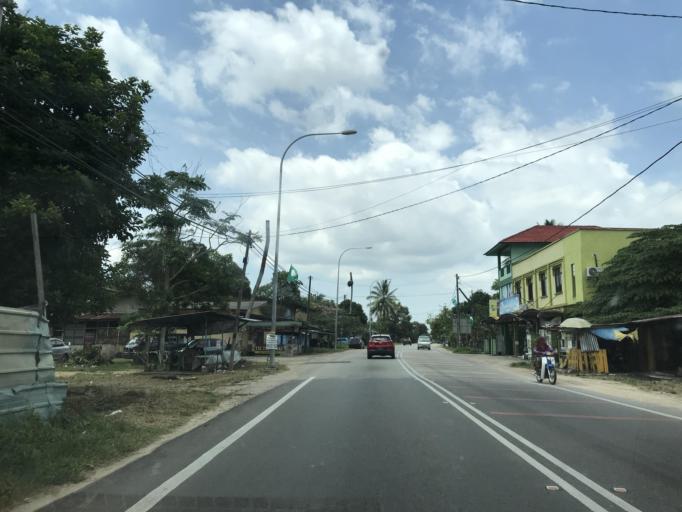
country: MY
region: Kelantan
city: Pasir Mas
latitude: 6.0525
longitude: 102.1885
